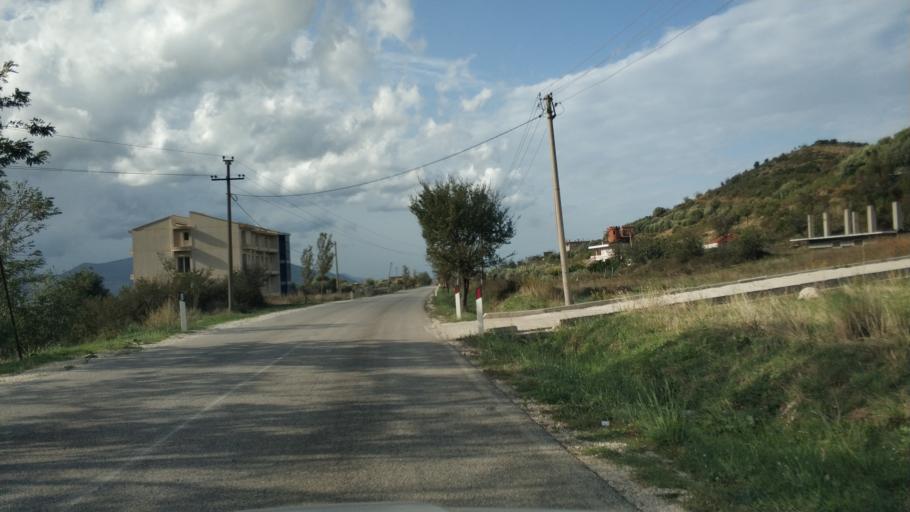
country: AL
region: Vlore
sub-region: Rrethi i Vlores
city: Orikum
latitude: 40.2985
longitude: 19.4872
